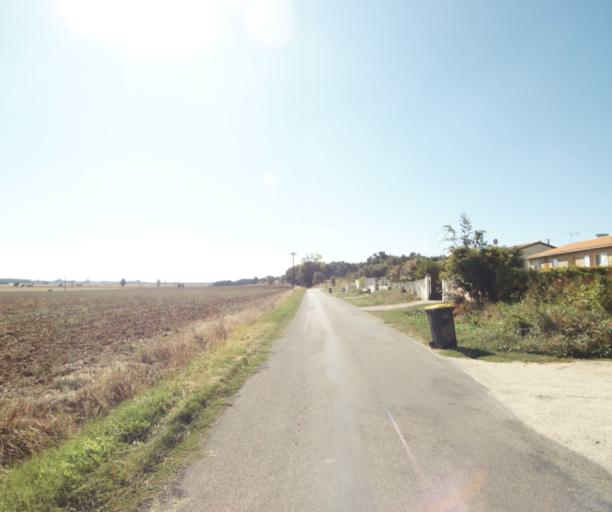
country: FR
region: Midi-Pyrenees
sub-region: Departement du Tarn-et-Garonne
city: Verdun-sur-Garonne
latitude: 43.8325
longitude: 1.2048
